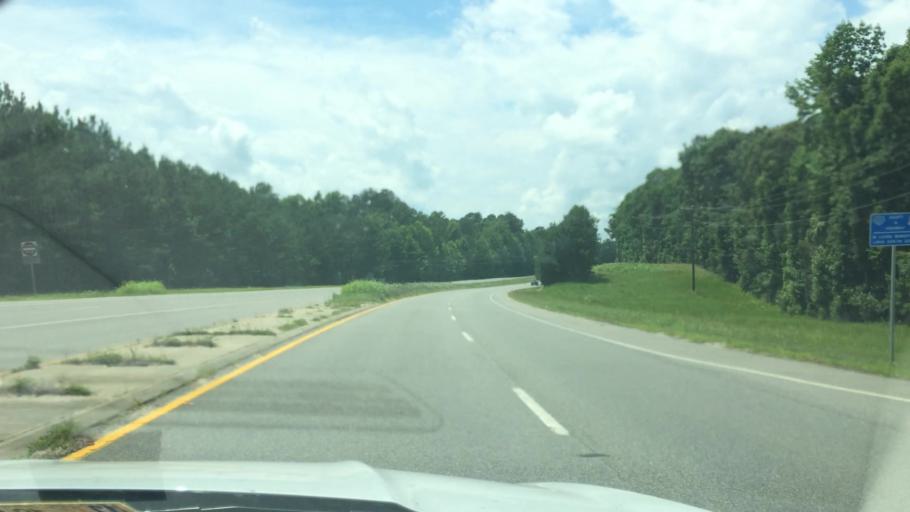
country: US
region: Virginia
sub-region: Middlesex County
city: Saluda
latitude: 37.5625
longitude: -76.6258
